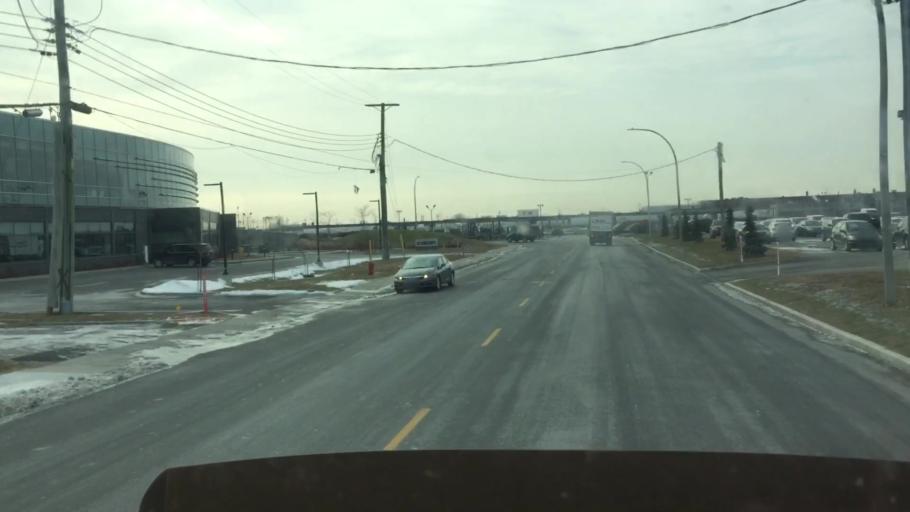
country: CA
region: Quebec
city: Dorval
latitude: 45.4673
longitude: -73.7208
